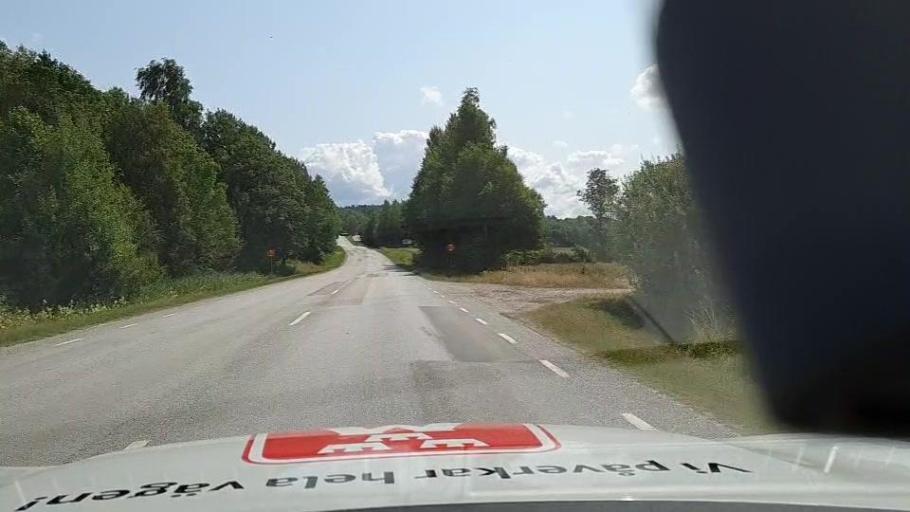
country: SE
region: Vaestra Goetaland
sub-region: Uddevalla Kommun
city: Ljungskile
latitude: 58.1859
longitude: 11.9514
